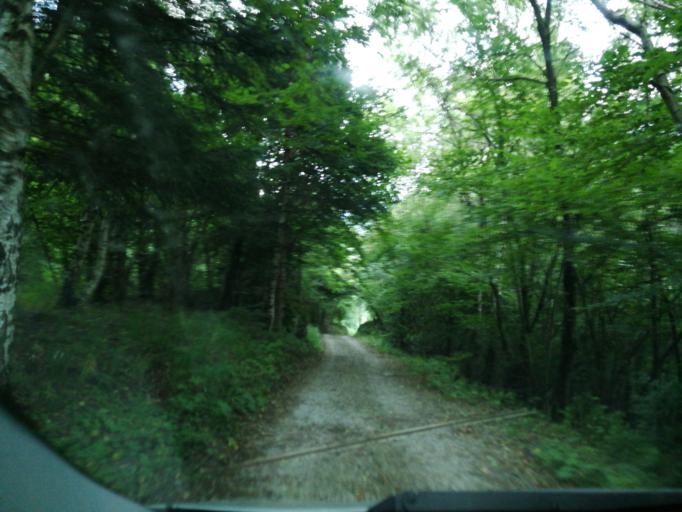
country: IT
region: Trentino-Alto Adige
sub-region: Provincia di Trento
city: Castel Condino
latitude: 45.9301
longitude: 10.6033
